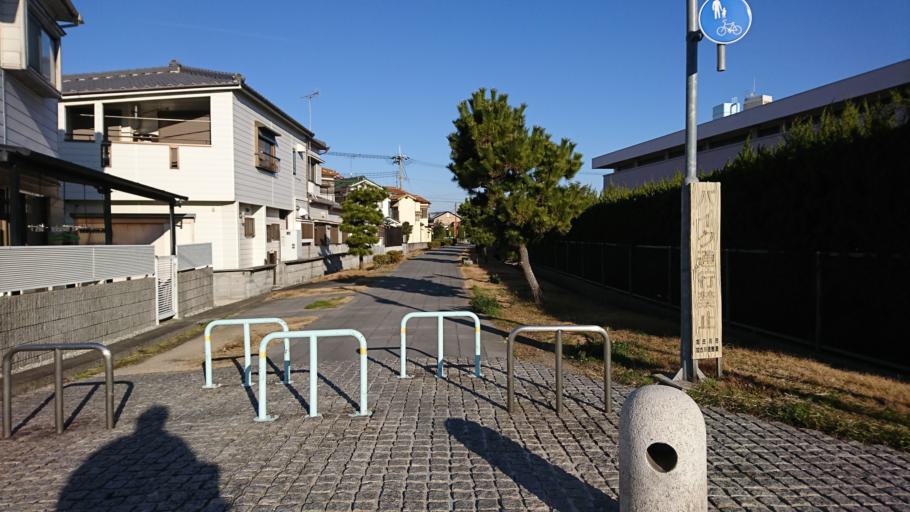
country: JP
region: Hyogo
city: Kakogawacho-honmachi
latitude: 34.7510
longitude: 134.8377
